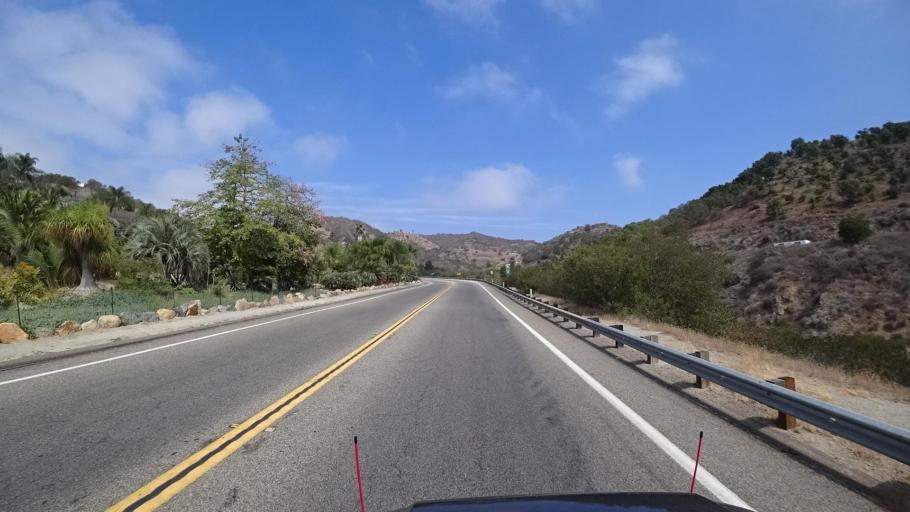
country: US
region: California
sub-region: San Diego County
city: Rainbow
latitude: 33.3888
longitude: -117.1777
